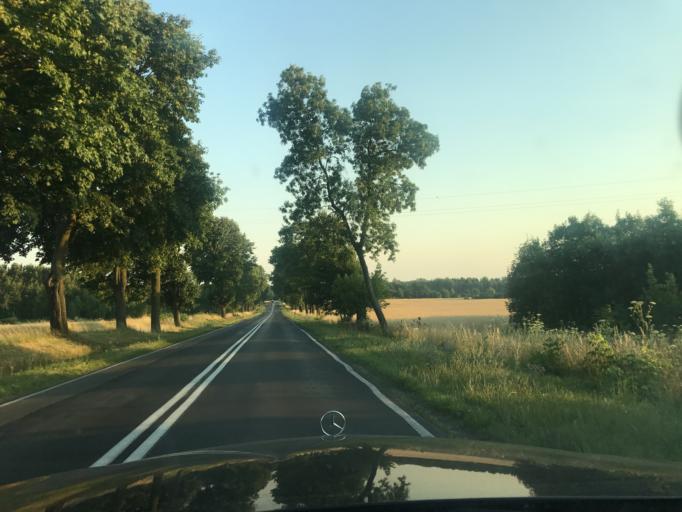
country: PL
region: Lublin Voivodeship
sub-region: Powiat lubartowski
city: Niedzwiada
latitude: 51.5051
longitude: 22.6622
